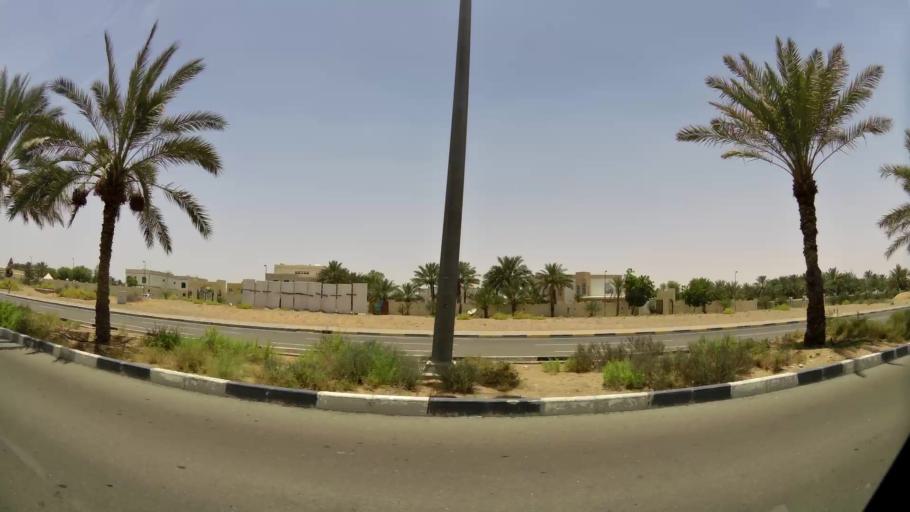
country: OM
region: Al Buraimi
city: Al Buraymi
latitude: 24.2630
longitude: 55.7204
